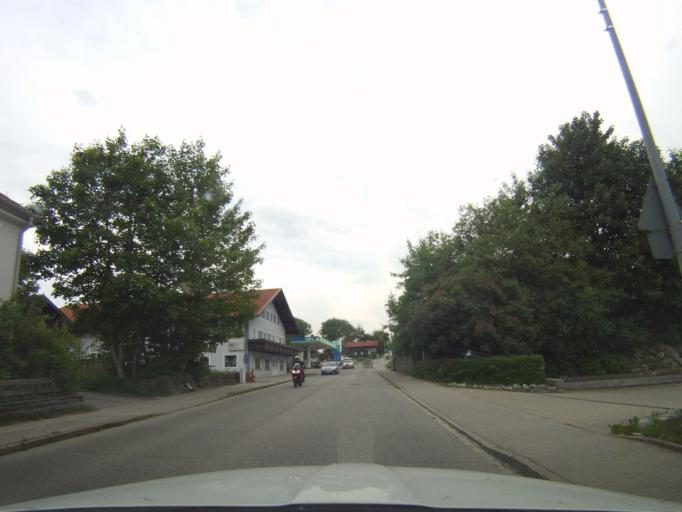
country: DE
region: Bavaria
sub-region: Swabia
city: Nesselwang
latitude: 47.6206
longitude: 10.5051
